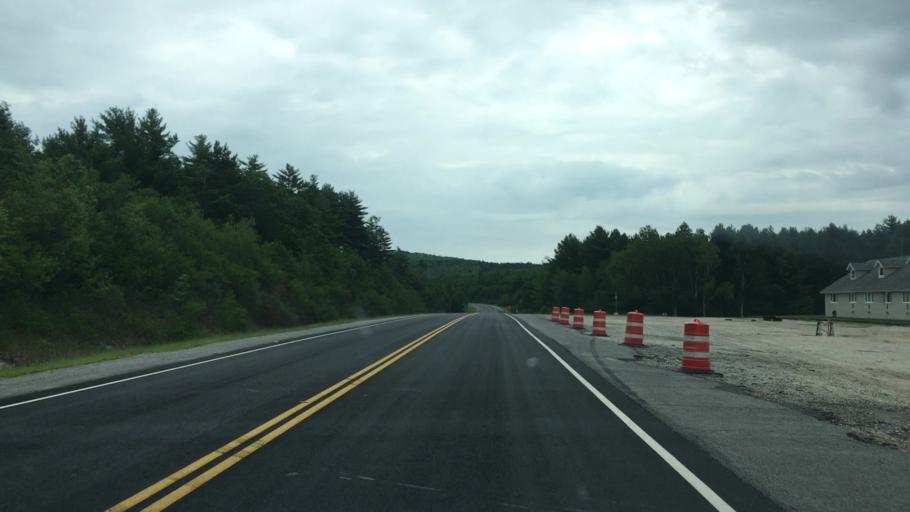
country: US
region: Maine
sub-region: Washington County
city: Cherryfield
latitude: 44.8788
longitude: -67.8700
